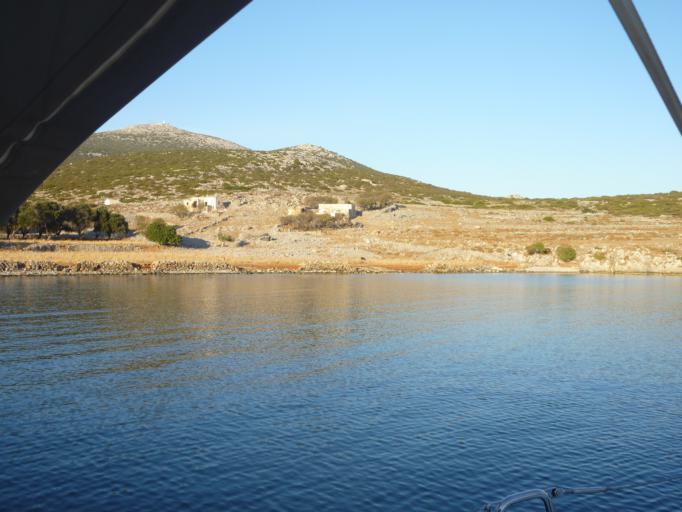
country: GR
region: South Aegean
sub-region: Nomos Dodekanisou
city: Astypalaia
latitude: 36.5855
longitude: 26.4237
